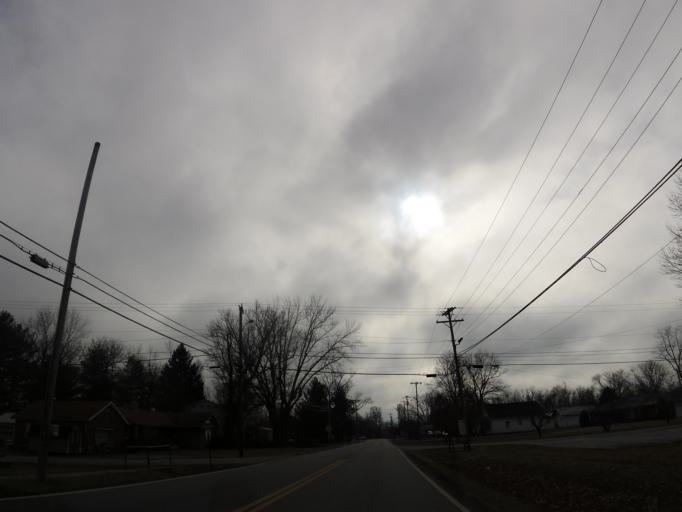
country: US
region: Kentucky
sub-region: Trimble County
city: Bedford
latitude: 38.6002
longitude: -85.3165
